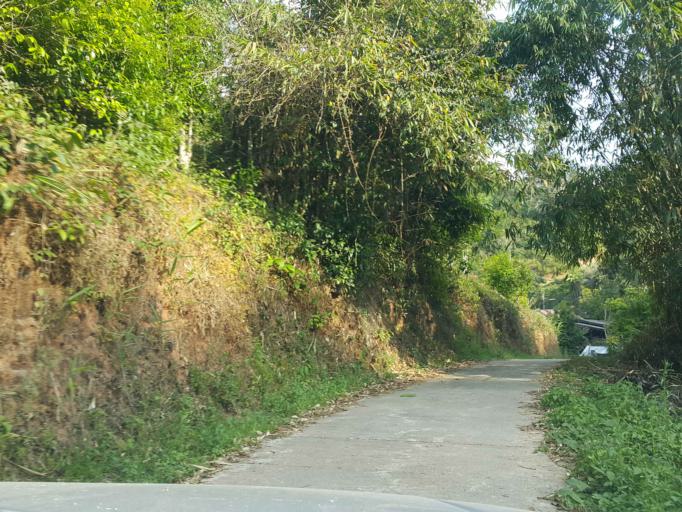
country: TH
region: Chiang Mai
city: Mae On
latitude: 18.9216
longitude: 99.3590
